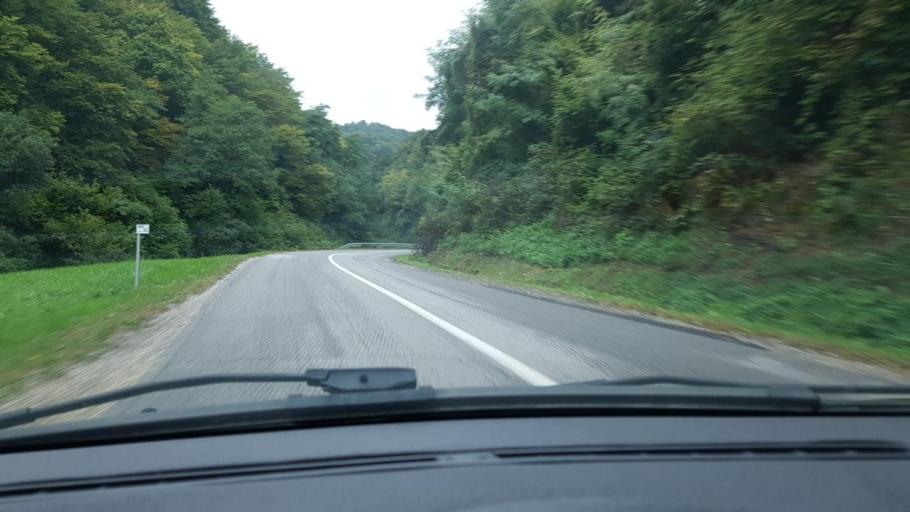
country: HR
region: Krapinsko-Zagorska
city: Marija Bistrica
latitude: 45.9404
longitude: 16.1103
